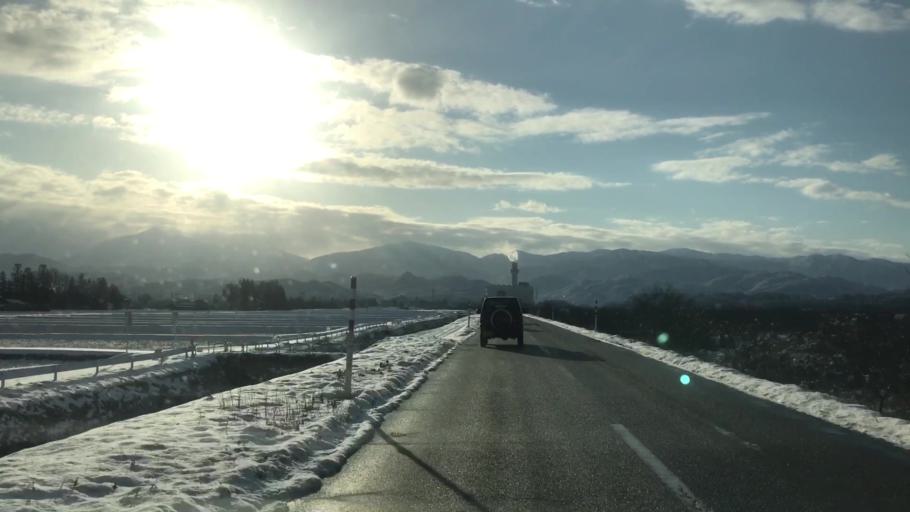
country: JP
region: Toyama
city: Kamiichi
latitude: 36.6351
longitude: 137.2929
